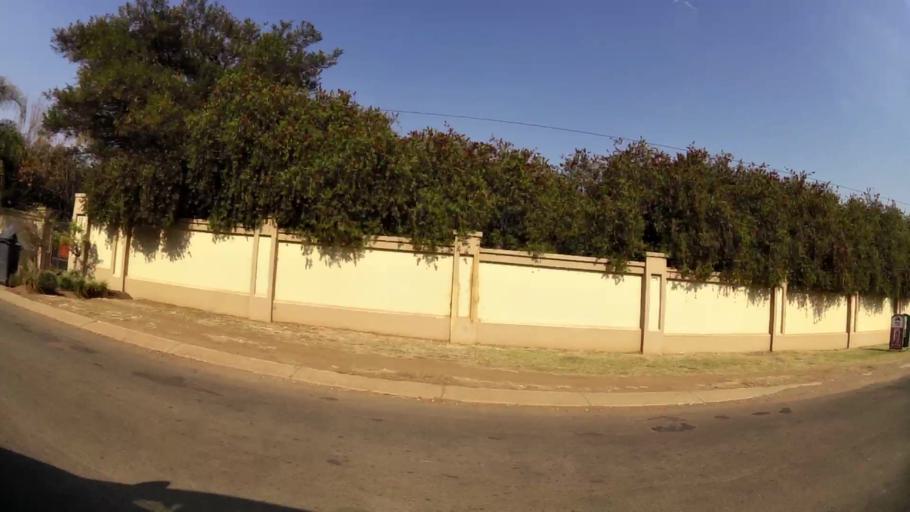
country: ZA
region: Gauteng
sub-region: City of Tshwane Metropolitan Municipality
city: Pretoria
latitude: -25.7644
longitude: 28.3457
